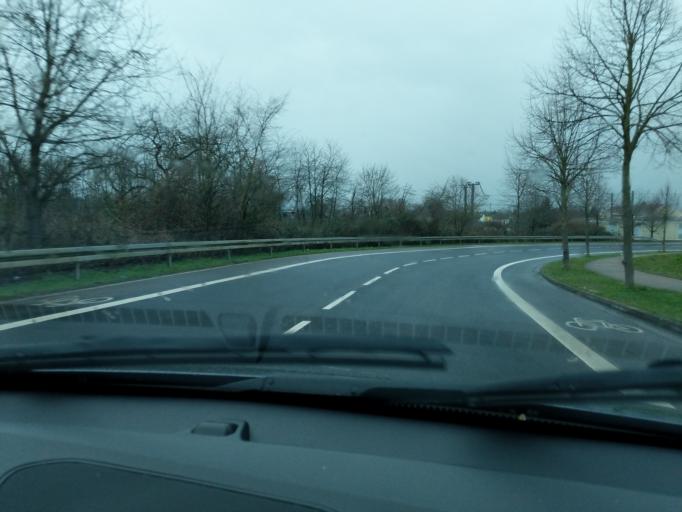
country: DE
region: Hesse
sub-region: Regierungsbezirk Darmstadt
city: Frankfurt am Main
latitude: 50.1497
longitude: 8.7022
